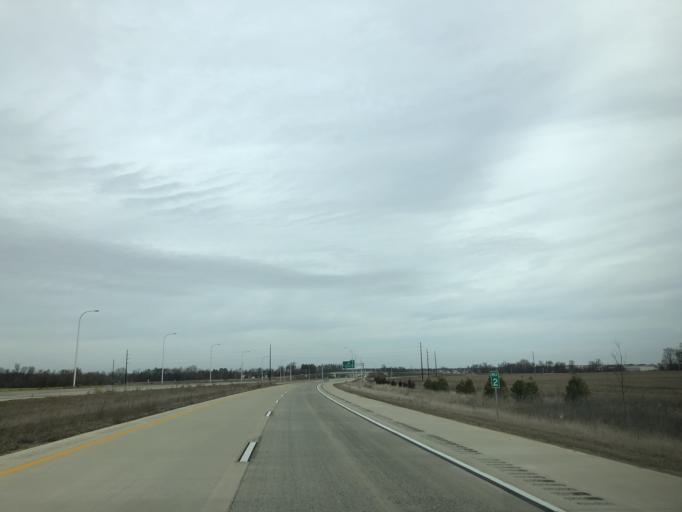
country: US
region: Delaware
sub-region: New Castle County
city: Middletown
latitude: 39.4390
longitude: -75.7572
